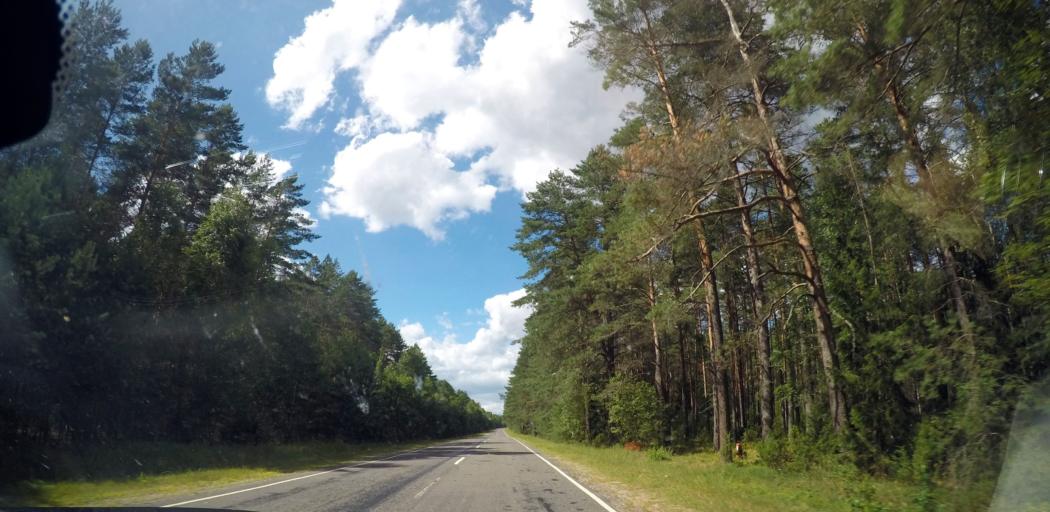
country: BY
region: Grodnenskaya
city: Skidal'
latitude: 53.8486
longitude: 24.2000
